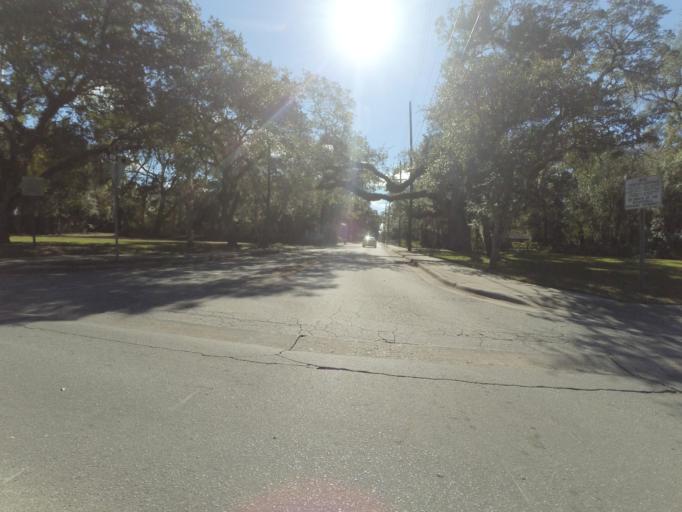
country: US
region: Florida
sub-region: Alachua County
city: Gainesville
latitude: 29.6558
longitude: -82.3371
